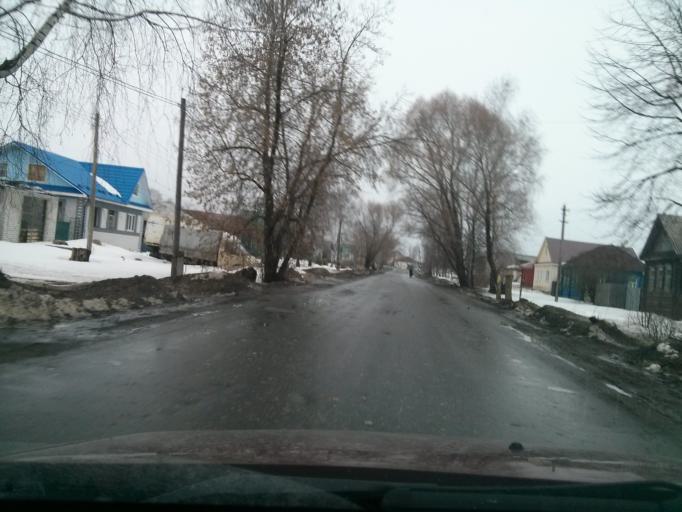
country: RU
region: Vladimir
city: Murom
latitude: 55.5432
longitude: 42.0258
